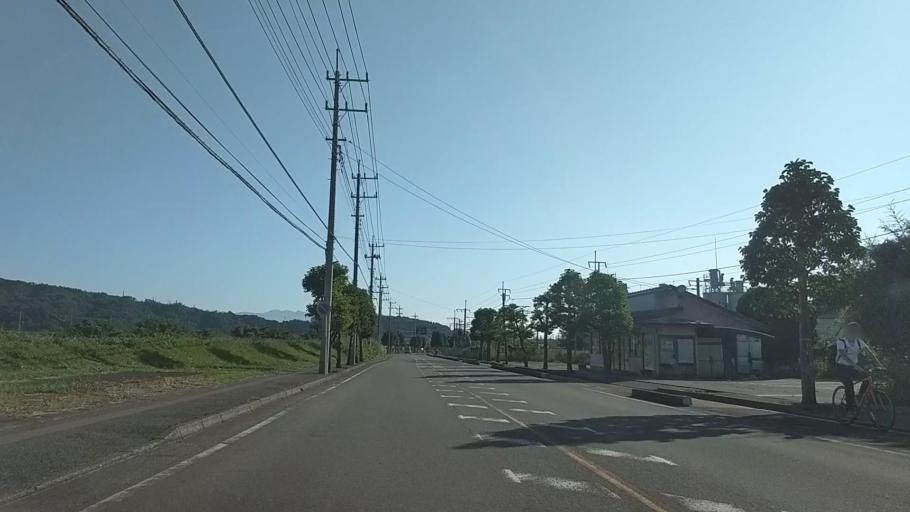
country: JP
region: Gunma
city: Annaka
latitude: 36.3305
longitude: 138.9085
